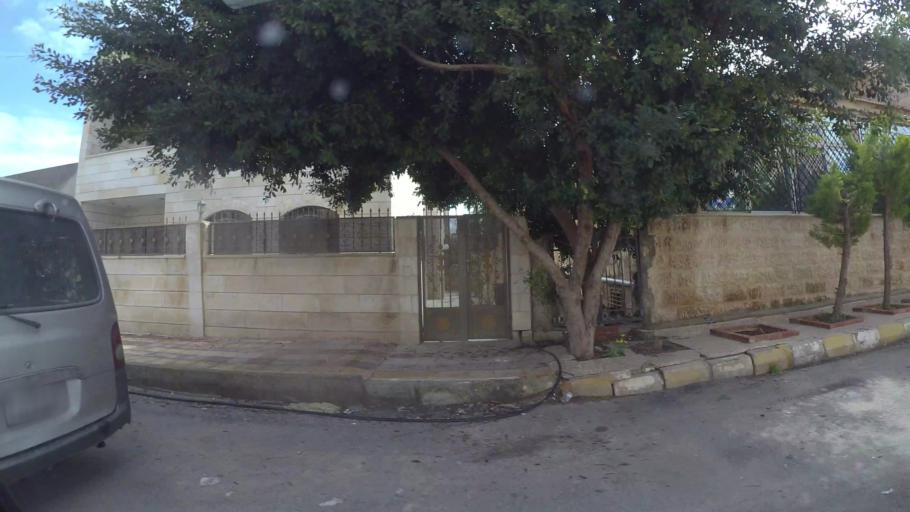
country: JO
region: Amman
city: Al Jubayhah
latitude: 32.0698
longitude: 35.8196
